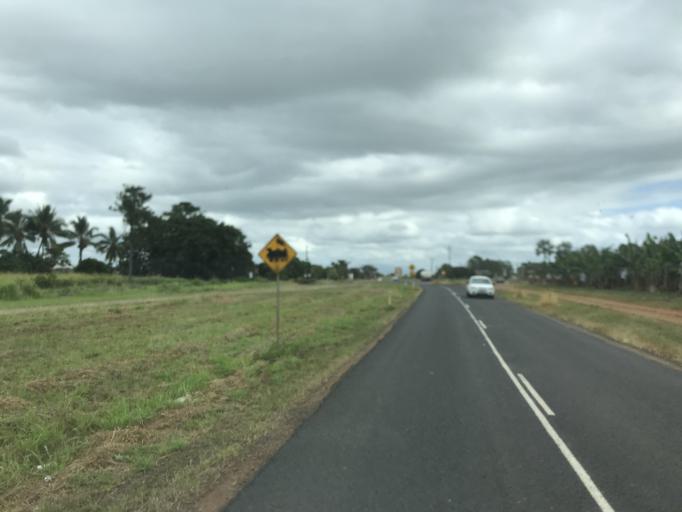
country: AU
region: Queensland
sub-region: Cassowary Coast
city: Innisfail
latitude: -17.6073
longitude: 146.0132
